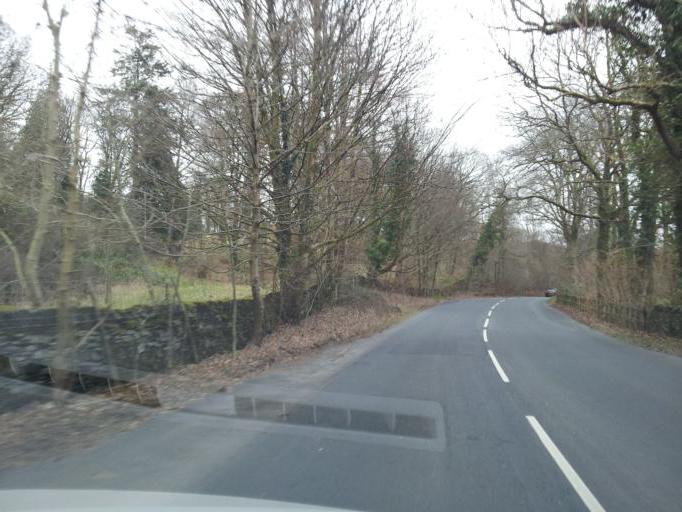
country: GB
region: England
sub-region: Cumbria
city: Ambleside
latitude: 54.4222
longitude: -2.9845
